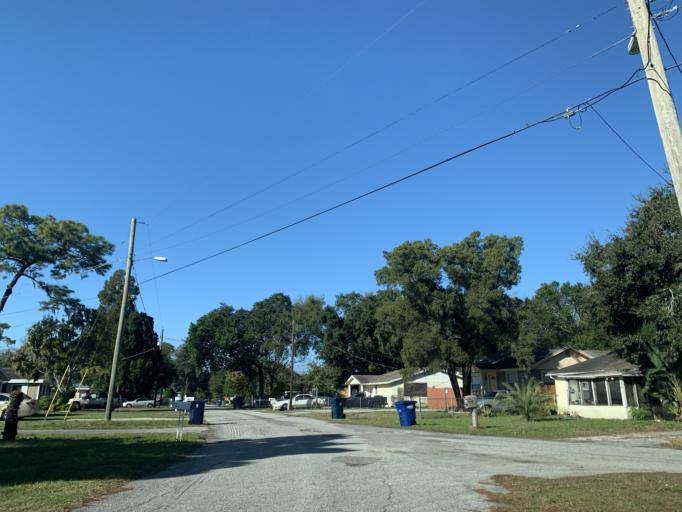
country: US
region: Florida
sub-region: Hillsborough County
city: Temple Terrace
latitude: 28.0226
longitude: -82.4115
